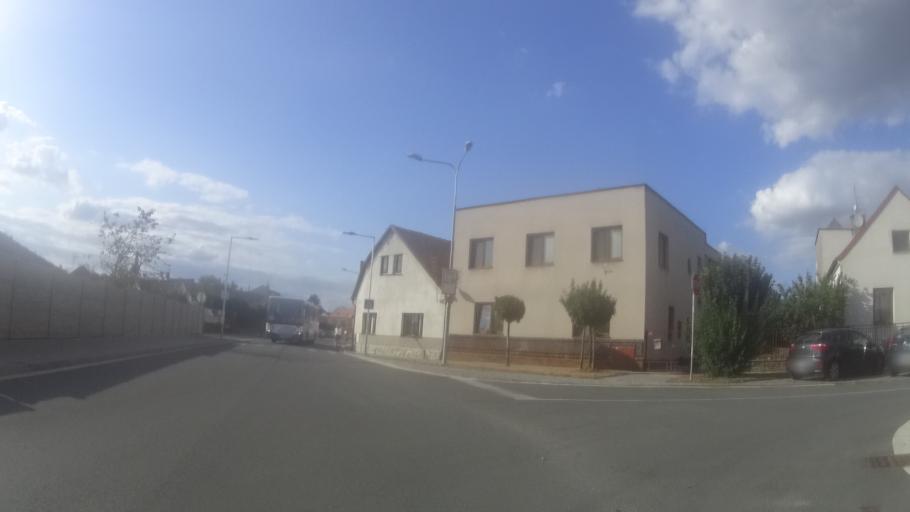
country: CZ
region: Kralovehradecky
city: Trebechovice pod Orebem
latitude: 50.1989
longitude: 15.9996
